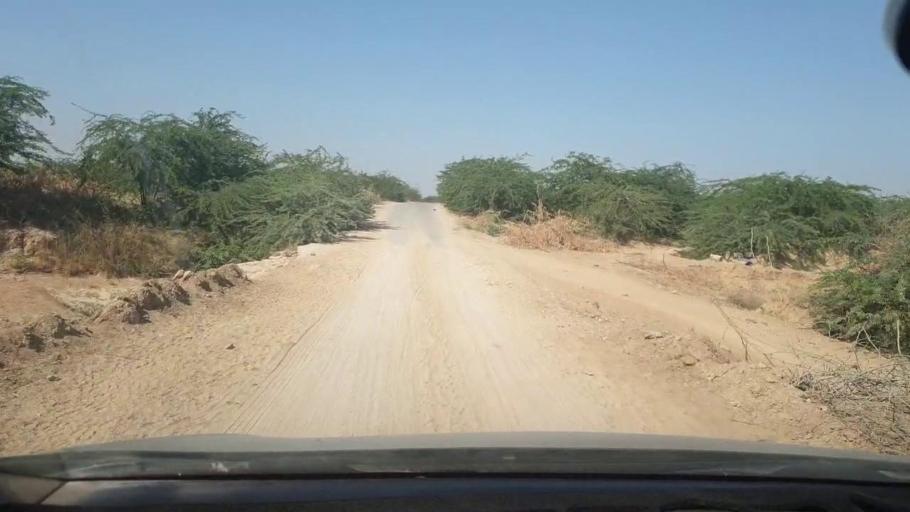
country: PK
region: Sindh
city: Malir Cantonment
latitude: 25.1592
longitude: 67.1642
